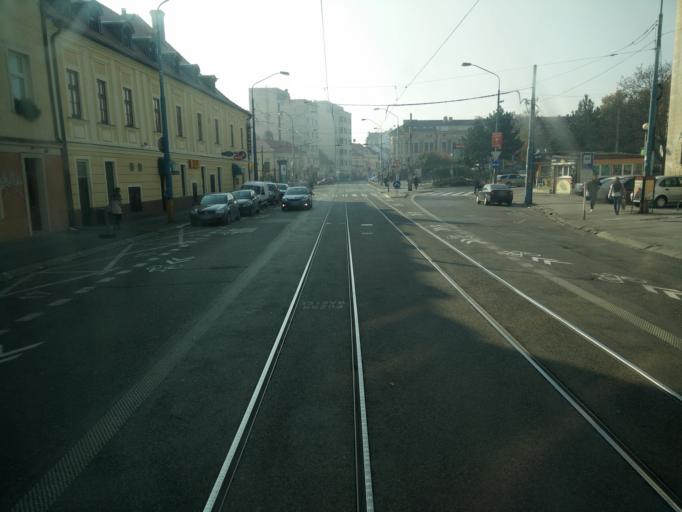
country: SK
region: Bratislavsky
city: Bratislava
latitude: 48.1499
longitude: 17.1144
